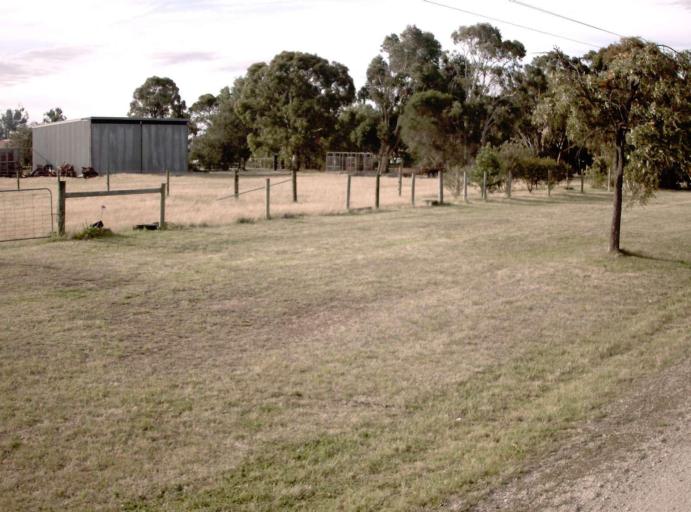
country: AU
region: Victoria
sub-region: Wellington
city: Sale
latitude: -37.9505
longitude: 146.9881
